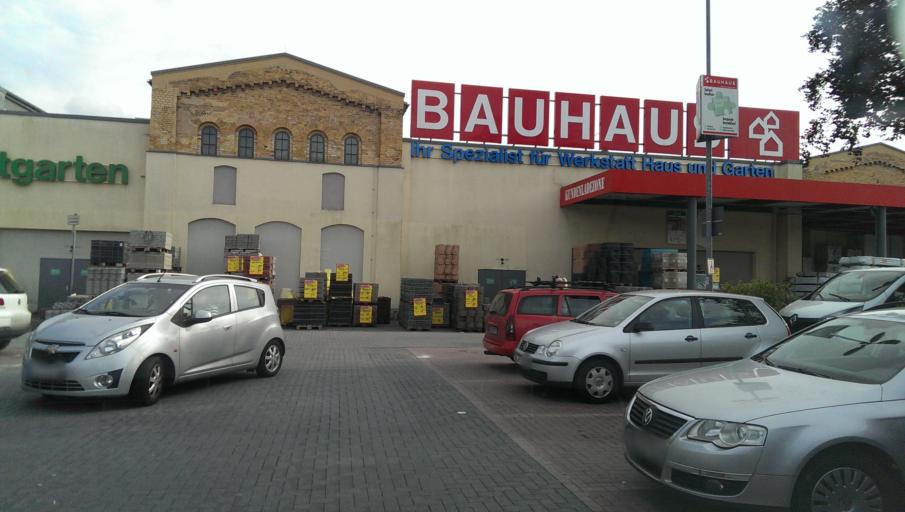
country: DE
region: Berlin
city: Schoneberg Bezirk
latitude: 52.4689
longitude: 13.3692
